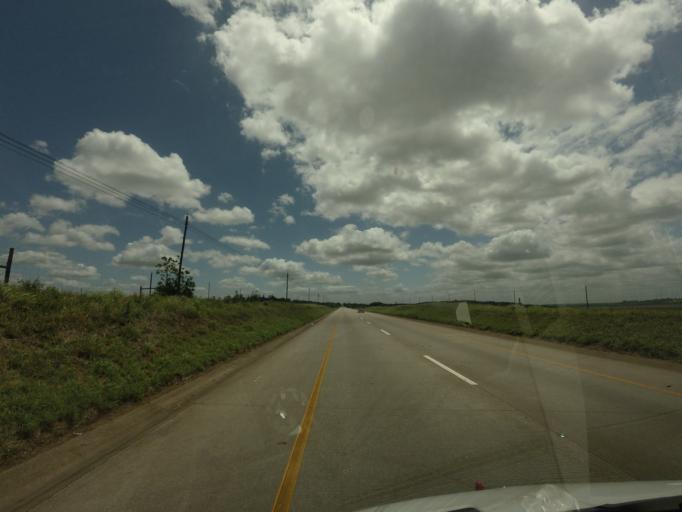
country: ZA
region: KwaZulu-Natal
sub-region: uMkhanyakude District Municipality
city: Mtubatuba
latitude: -28.4950
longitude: 32.1397
